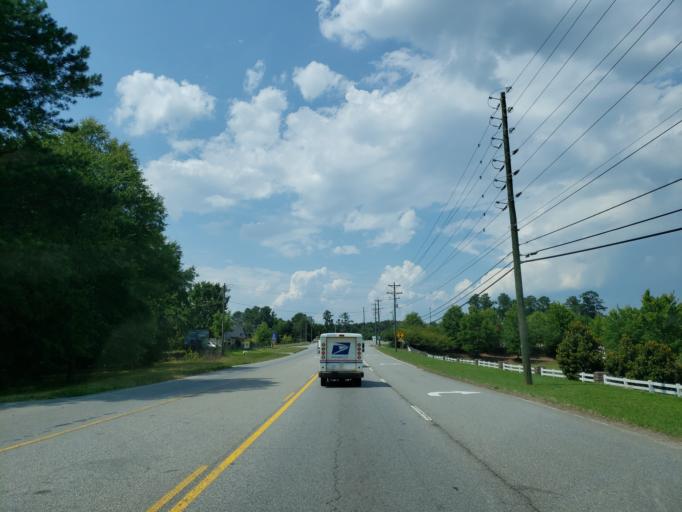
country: US
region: Georgia
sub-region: Fulton County
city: Milton
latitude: 34.1505
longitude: -84.2520
